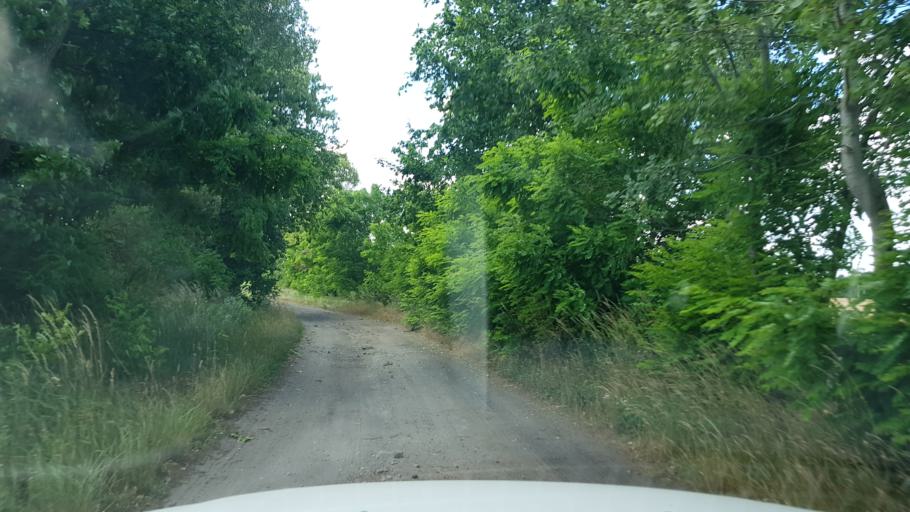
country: PL
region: West Pomeranian Voivodeship
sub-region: Powiat mysliborski
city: Debno
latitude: 52.7167
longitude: 14.6542
